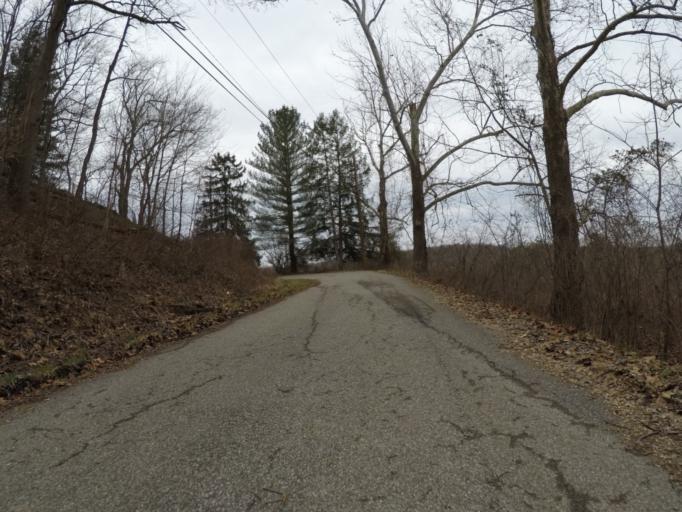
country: US
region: Ohio
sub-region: Lawrence County
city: Burlington
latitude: 38.3813
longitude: -82.5078
